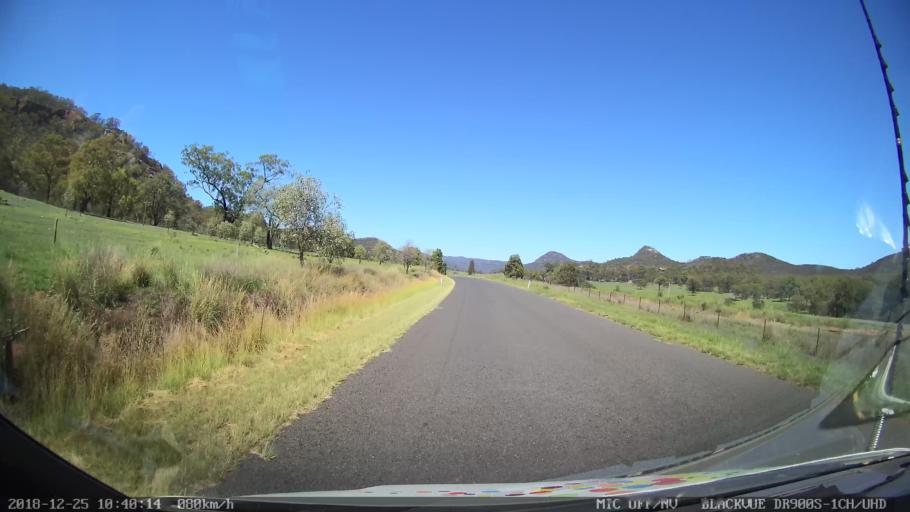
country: AU
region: New South Wales
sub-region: Upper Hunter Shire
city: Merriwa
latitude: -32.4061
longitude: 150.3454
